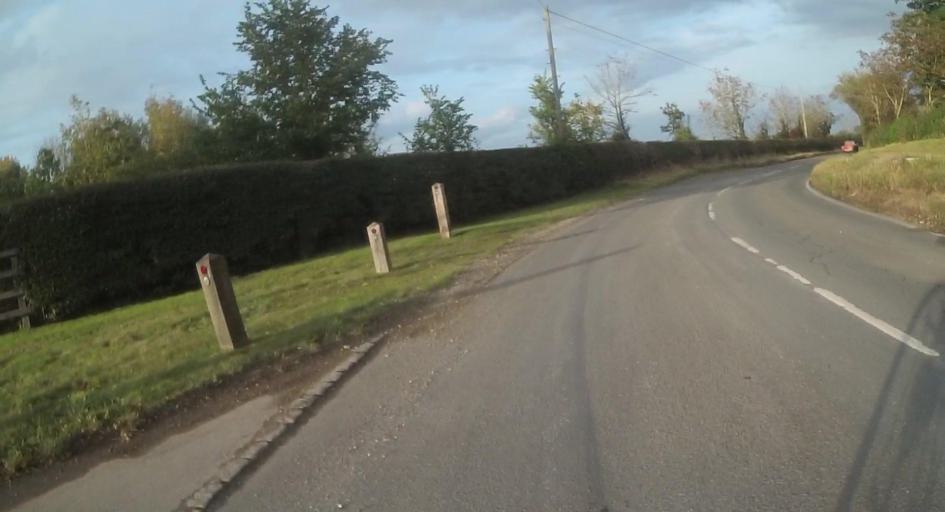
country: GB
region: England
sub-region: Hampshire
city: Tadley
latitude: 51.3817
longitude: -1.1673
